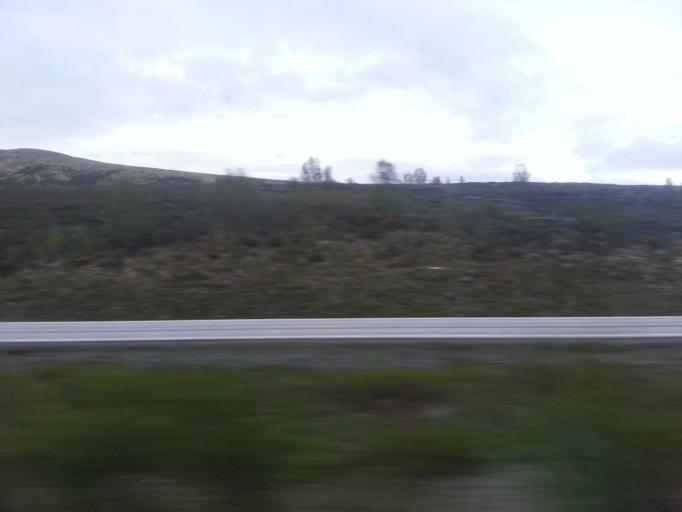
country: NO
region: Sor-Trondelag
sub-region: Oppdal
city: Oppdal
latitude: 62.2468
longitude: 9.5373
